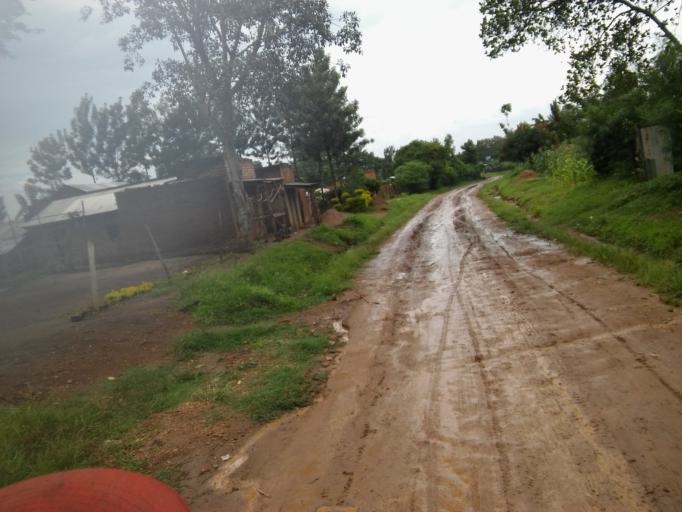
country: UG
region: Eastern Region
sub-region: Mbale District
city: Mbale
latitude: 1.0327
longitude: 34.2001
